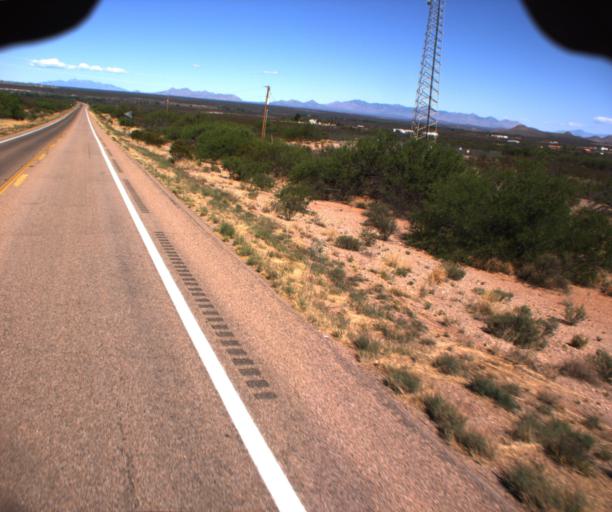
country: US
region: Arizona
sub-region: Cochise County
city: Sierra Vista Southeast
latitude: 31.5493
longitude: -110.1066
